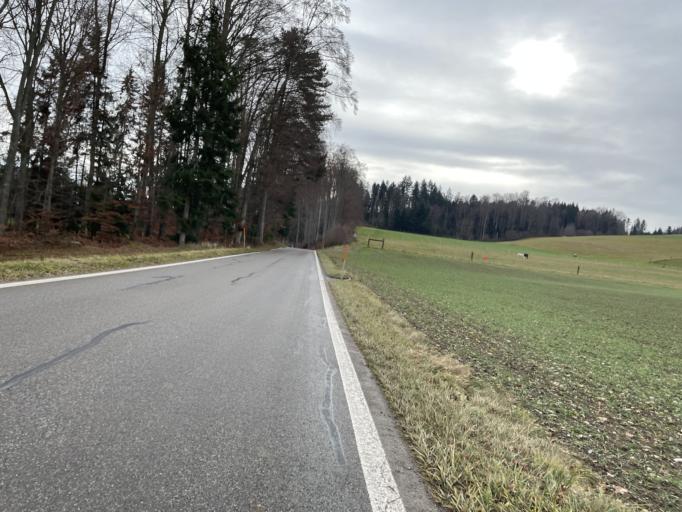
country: CH
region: Bern
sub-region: Bern-Mittelland District
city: Munsingen
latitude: 46.8557
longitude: 7.5420
